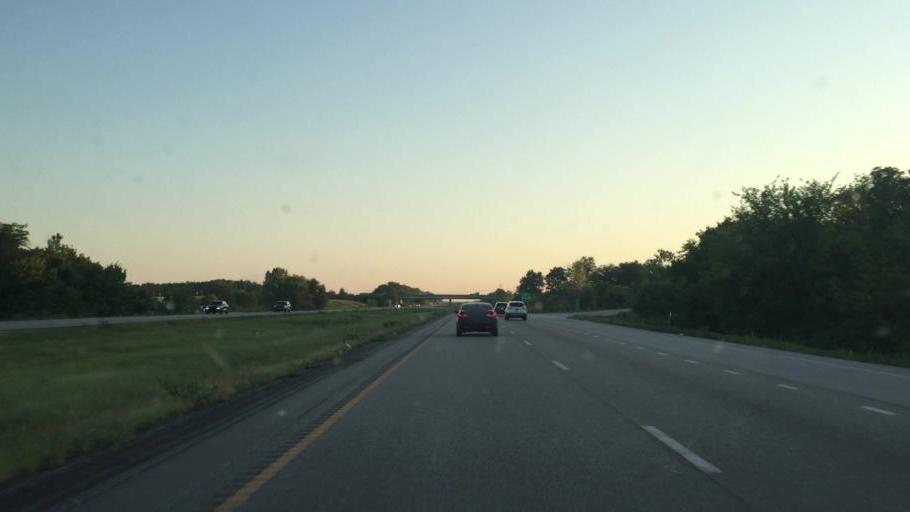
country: US
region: Missouri
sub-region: Clay County
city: Pleasant Valley
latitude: 39.2827
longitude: -94.5101
